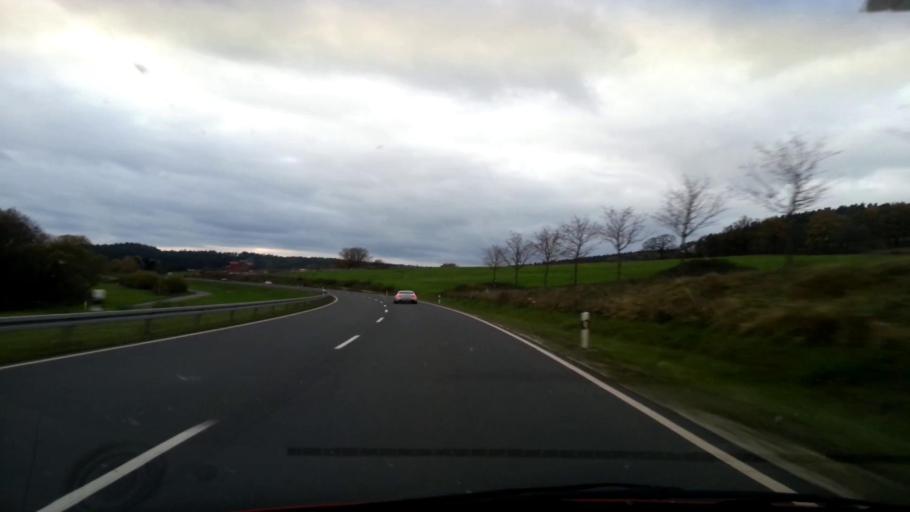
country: DE
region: Bavaria
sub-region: Upper Franconia
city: Schneckenlohe
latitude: 50.2136
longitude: 11.2080
